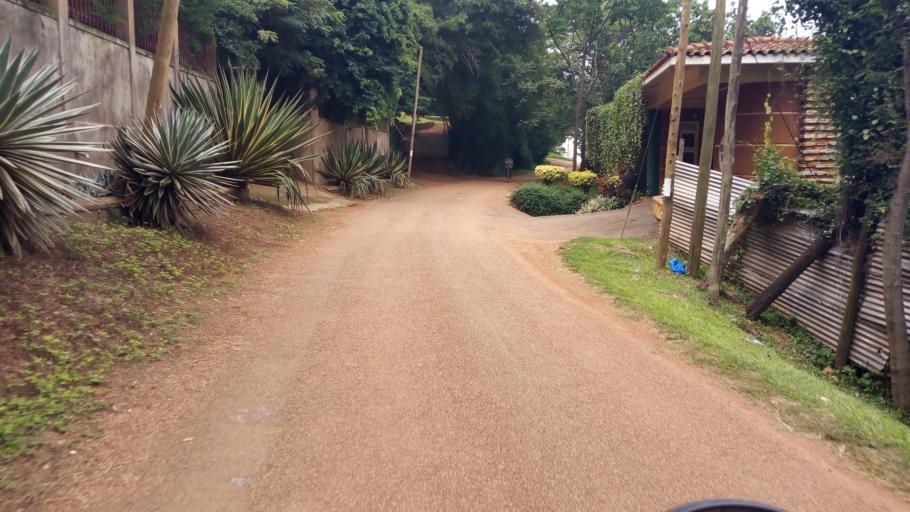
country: UG
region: Central Region
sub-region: Wakiso District
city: Kireka
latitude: 0.3248
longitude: 32.6300
